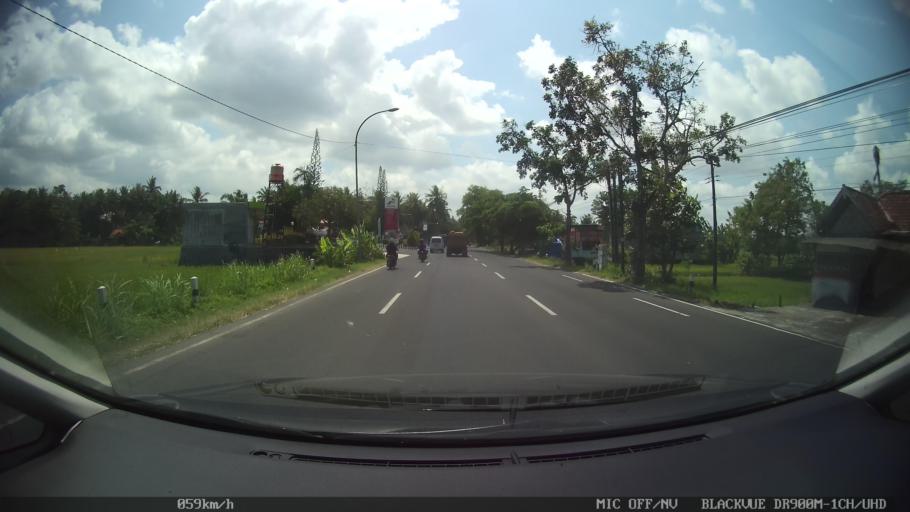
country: ID
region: Daerah Istimewa Yogyakarta
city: Pandak
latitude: -7.9150
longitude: 110.2864
